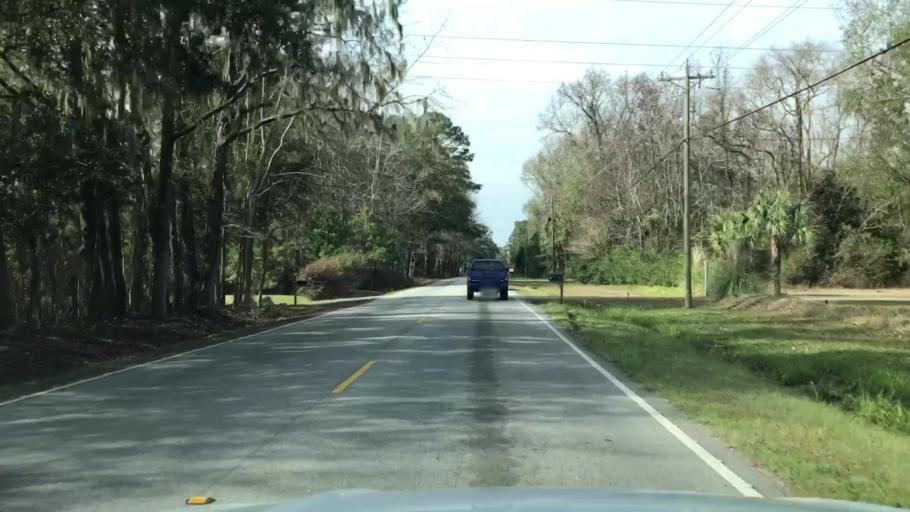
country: US
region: South Carolina
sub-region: Charleston County
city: Shell Point
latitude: 32.7788
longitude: -80.1007
